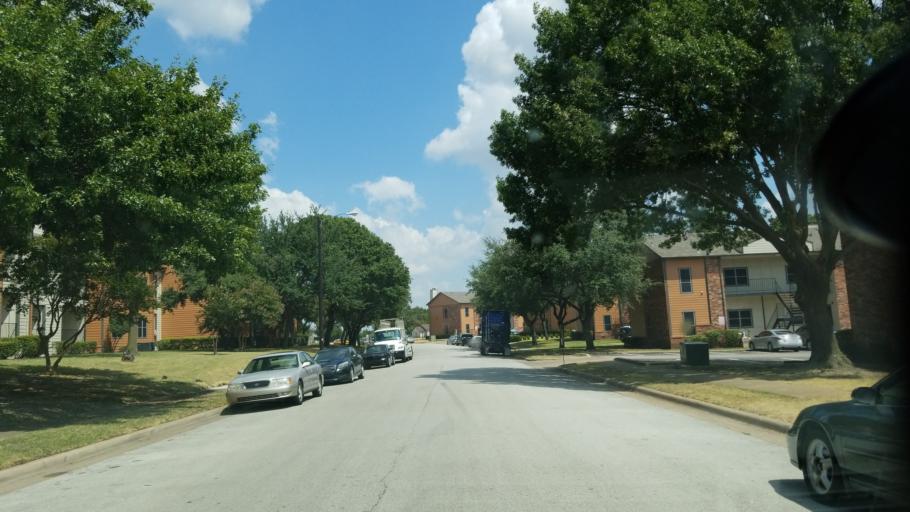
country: US
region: Texas
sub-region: Dallas County
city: Cockrell Hill
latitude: 32.6926
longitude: -96.8874
